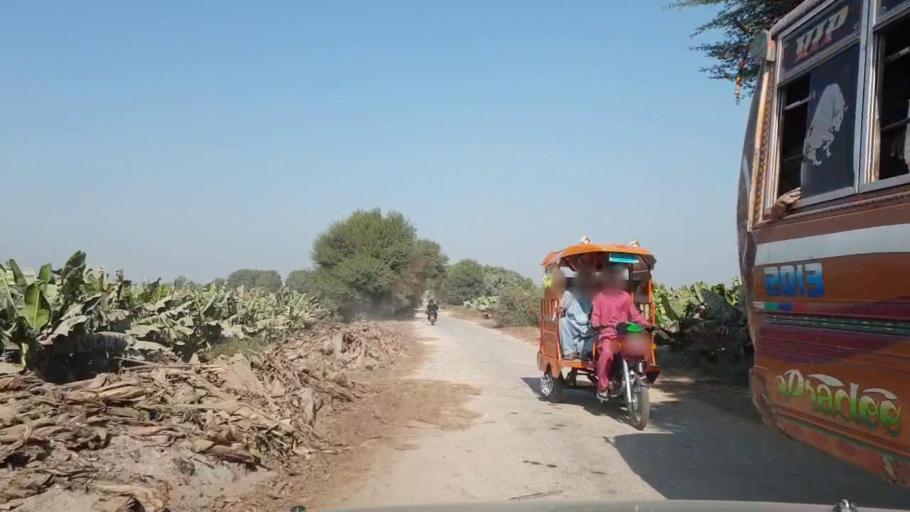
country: PK
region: Sindh
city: Matiari
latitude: 25.6040
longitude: 68.5986
